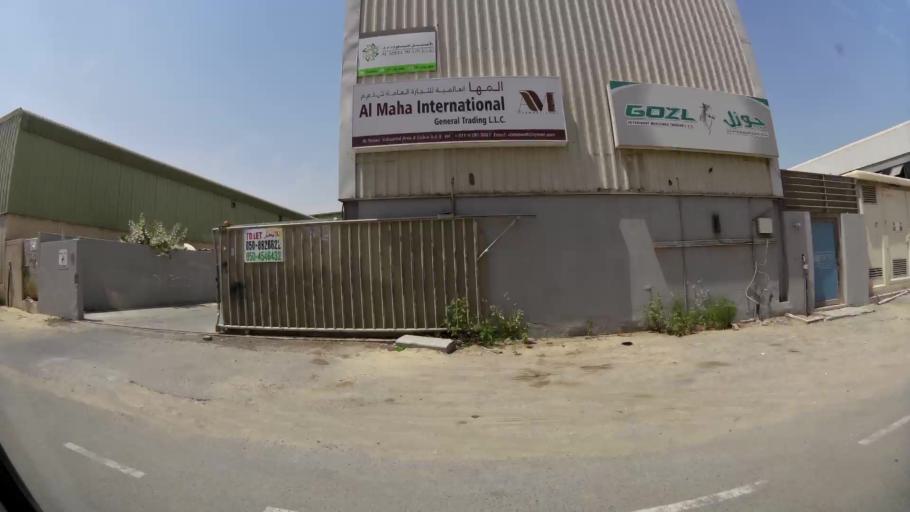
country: AE
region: Ash Shariqah
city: Sharjah
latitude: 25.2951
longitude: 55.4019
